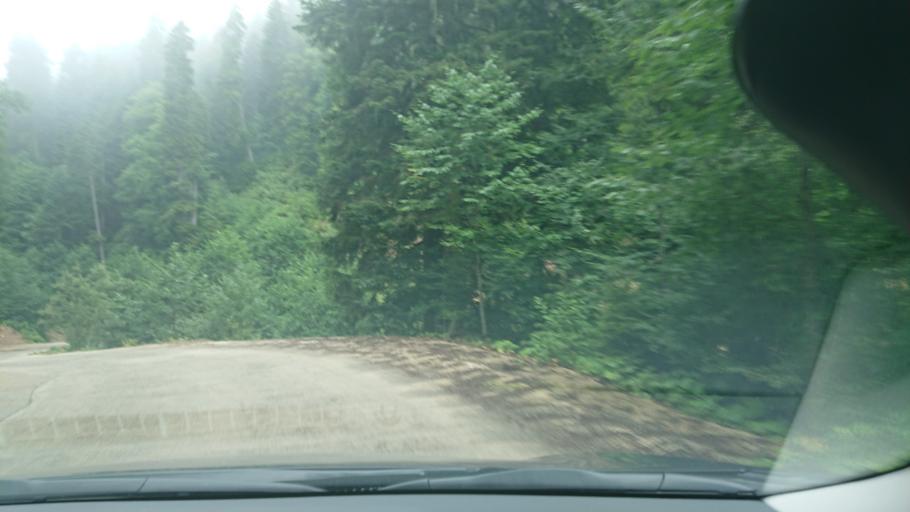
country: TR
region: Gumushane
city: Kurtun
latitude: 40.6585
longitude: 39.0200
